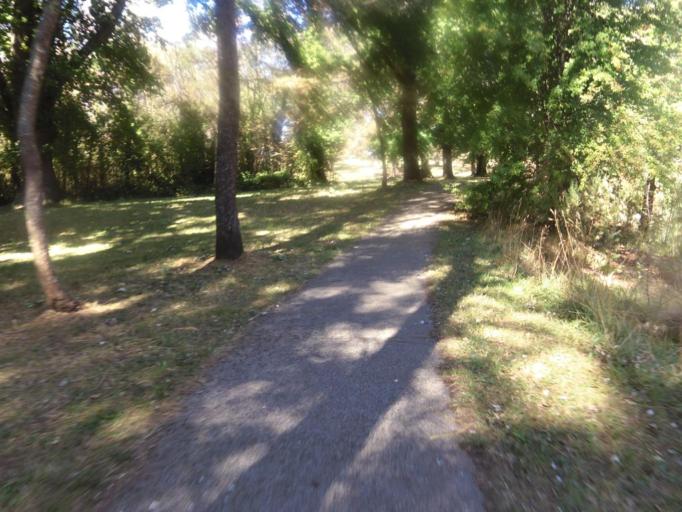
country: AU
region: Victoria
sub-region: Mount Alexander
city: Castlemaine
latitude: -37.2518
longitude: 144.4453
